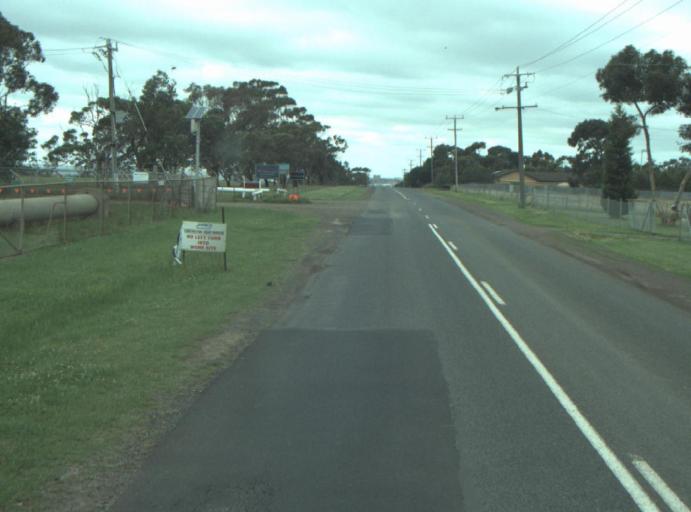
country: AU
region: Victoria
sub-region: Greater Geelong
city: Bell Post Hill
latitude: -38.0660
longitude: 144.3265
